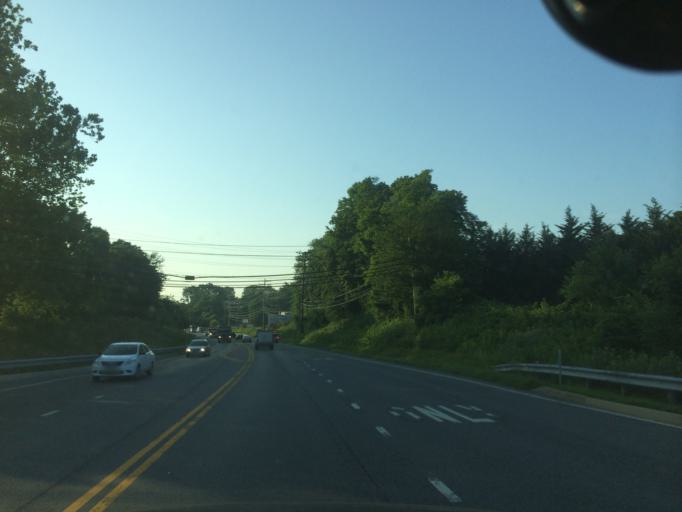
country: US
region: Maryland
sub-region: Carroll County
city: Eldersburg
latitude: 39.4129
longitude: -76.9789
